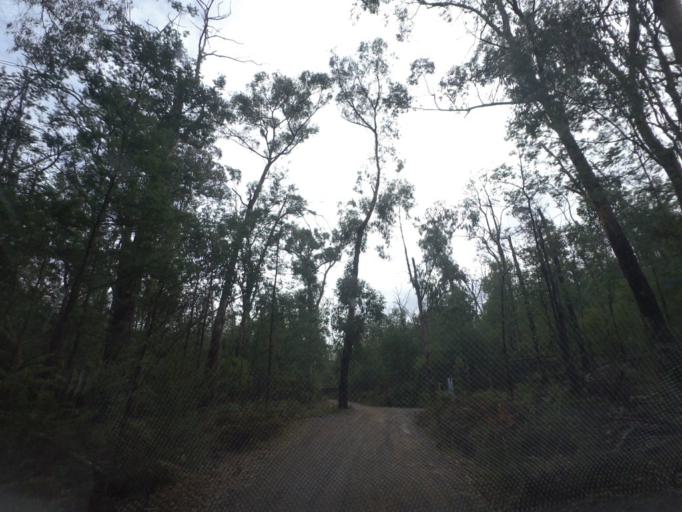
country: AU
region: Victoria
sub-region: Yarra Ranges
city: Healesville
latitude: -37.6316
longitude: 145.5362
